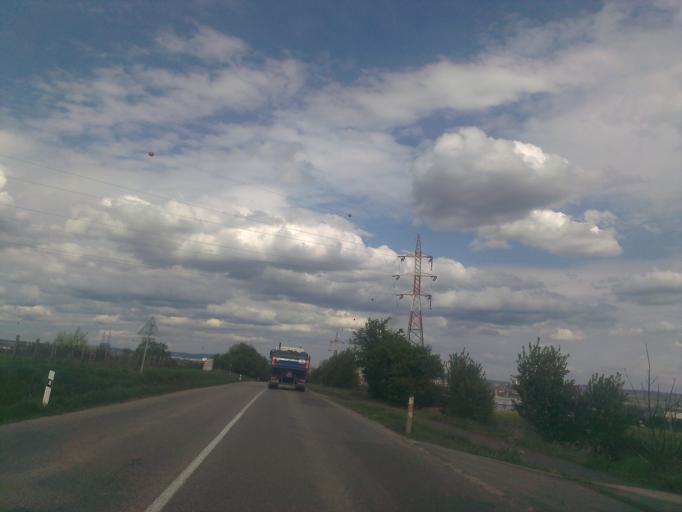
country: CZ
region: South Moravian
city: Modrice
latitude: 49.1198
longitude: 16.5965
